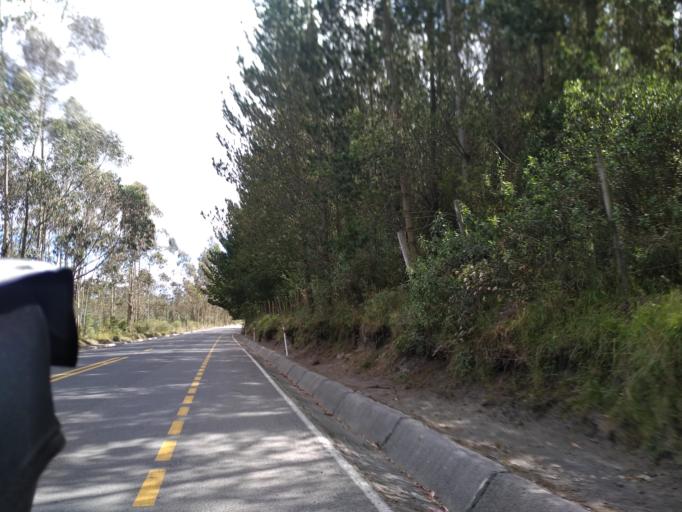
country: EC
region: Cotopaxi
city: Saquisili
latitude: -0.6973
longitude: -78.5720
